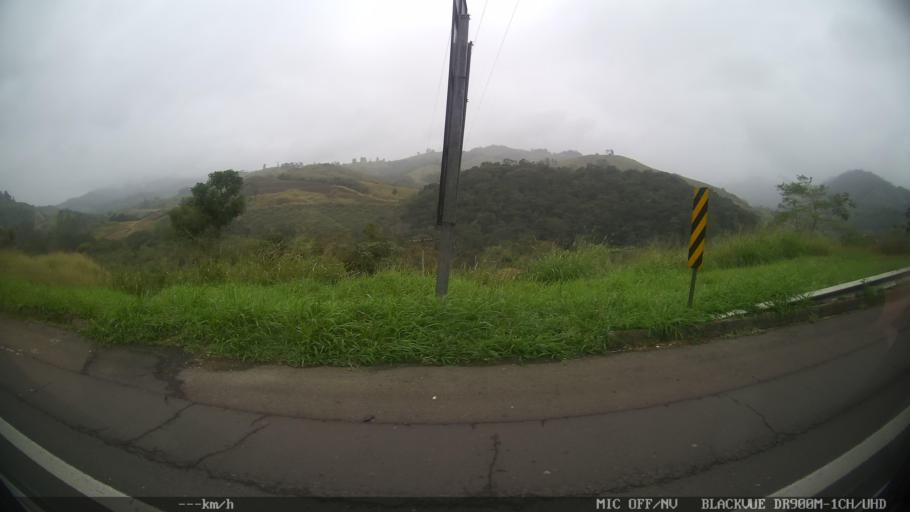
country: BR
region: Sao Paulo
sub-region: Cajati
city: Cajati
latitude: -24.7833
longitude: -48.2040
